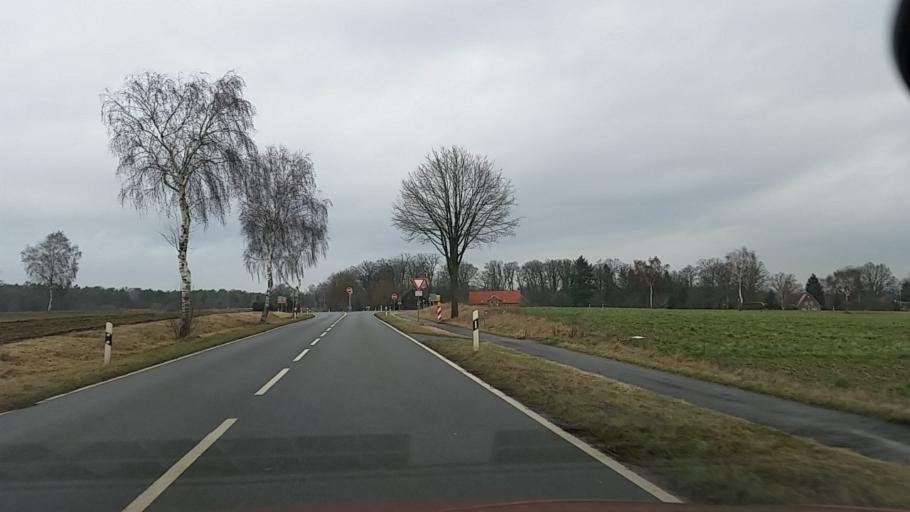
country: DE
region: Lower Saxony
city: Bispingen
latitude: 53.1258
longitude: 9.9995
